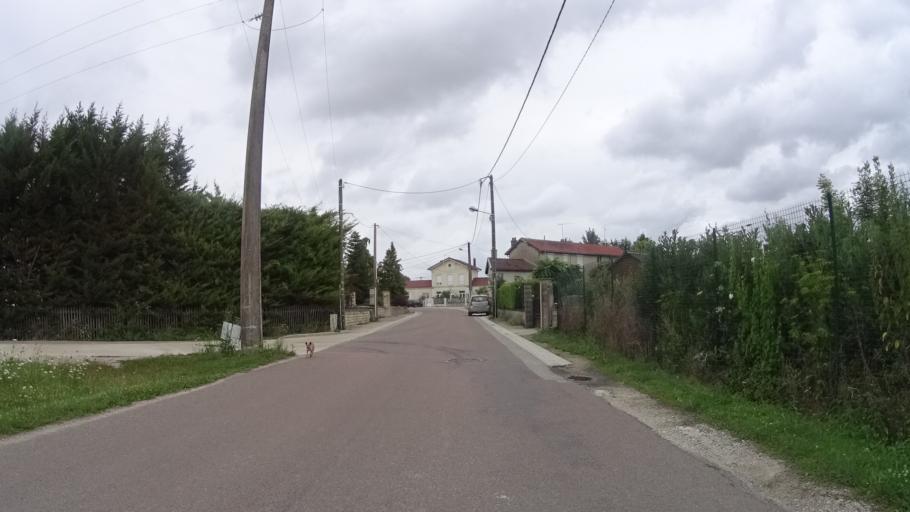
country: FR
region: Champagne-Ardenne
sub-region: Departement de l'Aube
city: Verrieres
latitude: 48.2309
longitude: 4.1313
